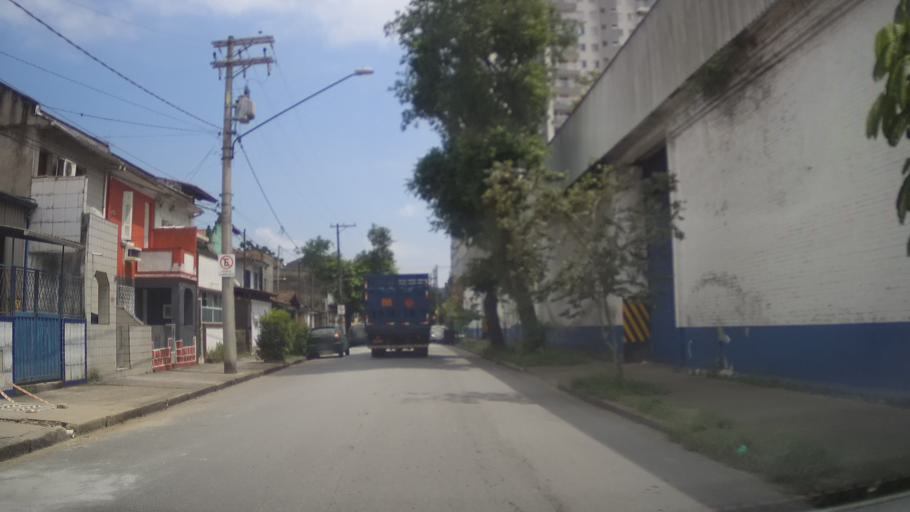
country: BR
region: Sao Paulo
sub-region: Santos
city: Santos
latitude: -23.9483
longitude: -46.3182
